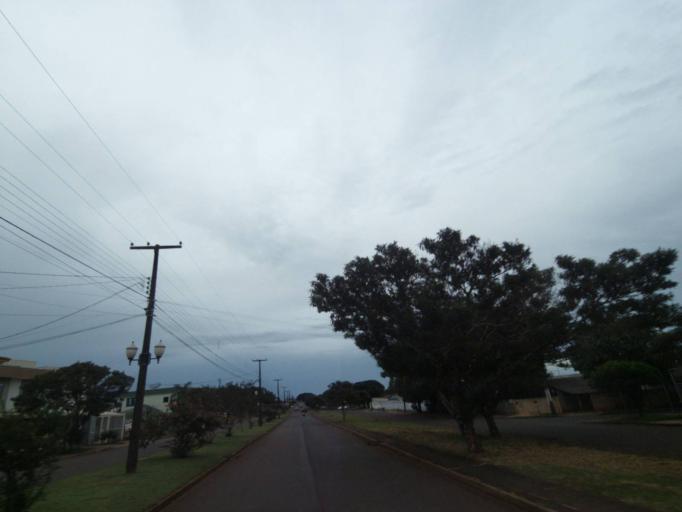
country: BR
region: Parana
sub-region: Campo Mourao
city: Campo Mourao
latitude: -24.0255
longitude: -52.3566
